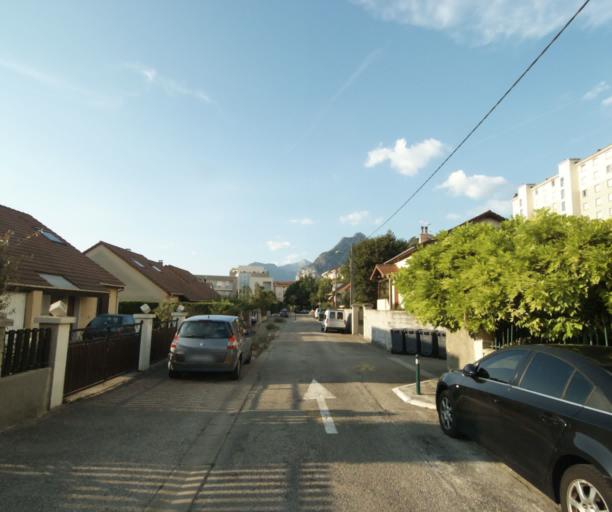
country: FR
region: Rhone-Alpes
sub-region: Departement de l'Isere
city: Seyssinet-Pariset
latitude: 45.1864
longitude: 5.6993
